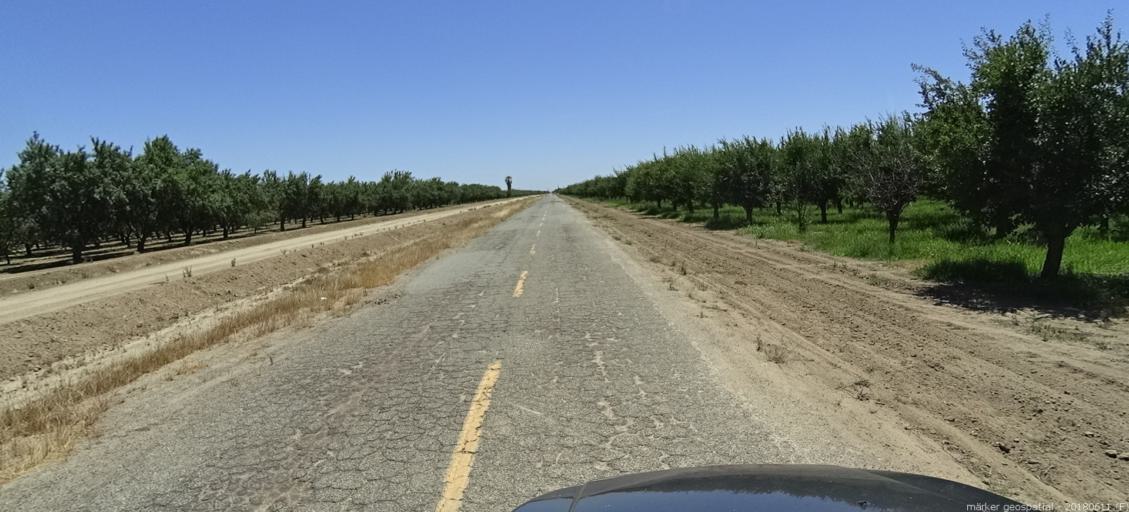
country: US
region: California
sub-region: Madera County
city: Fairmead
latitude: 37.0609
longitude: -120.2115
